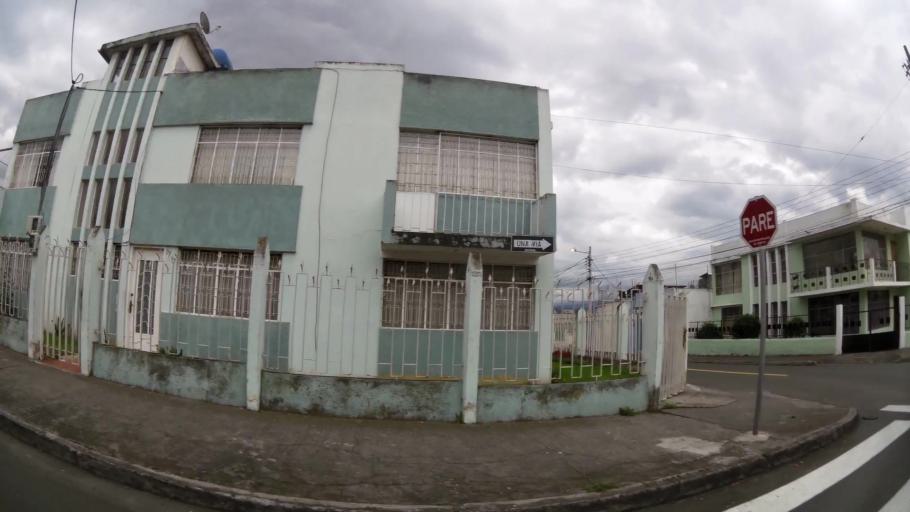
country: EC
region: Tungurahua
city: Ambato
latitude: -1.2369
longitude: -78.6146
